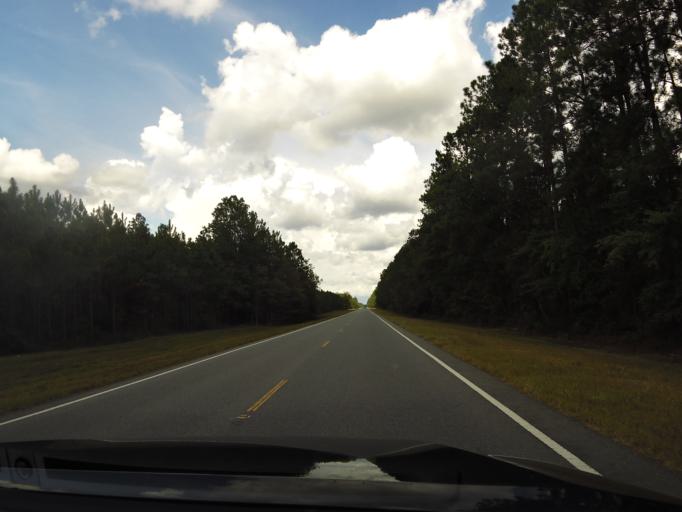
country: US
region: Georgia
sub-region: Charlton County
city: Folkston
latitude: 30.9753
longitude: -82.0249
